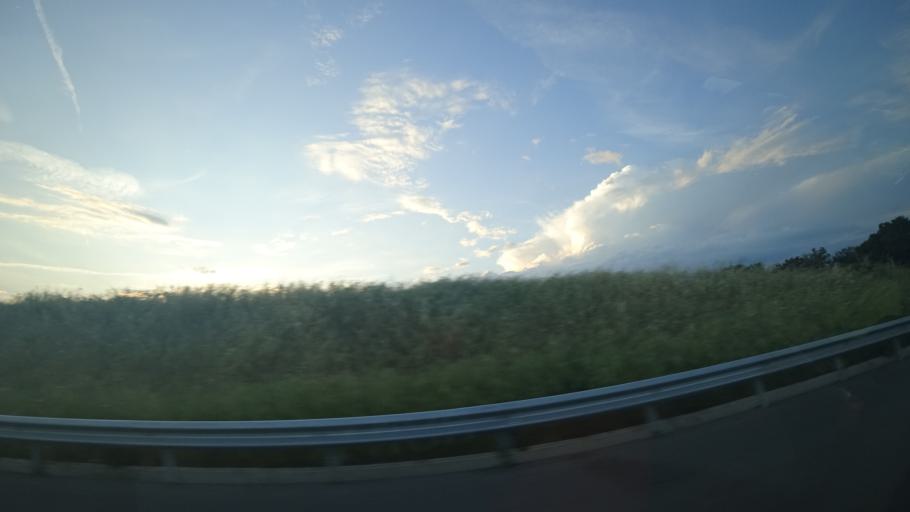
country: FR
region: Languedoc-Roussillon
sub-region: Departement de l'Herault
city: Boujan-sur-Libron
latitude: 43.3721
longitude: 3.2874
